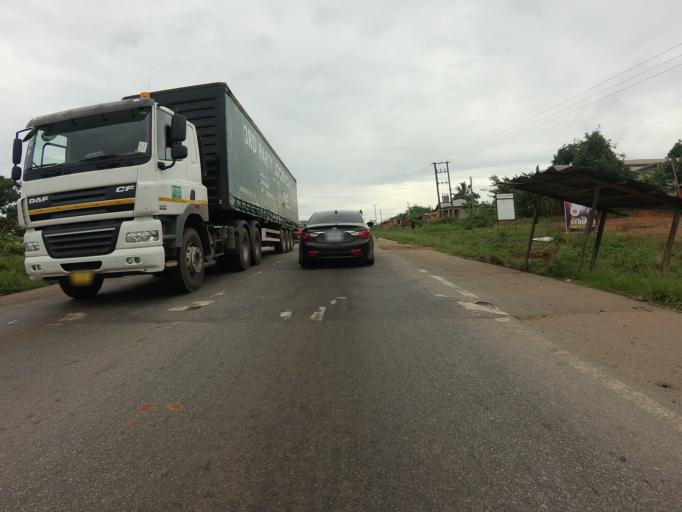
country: GH
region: Eastern
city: Nkawkaw
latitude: 6.4766
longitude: -0.6557
